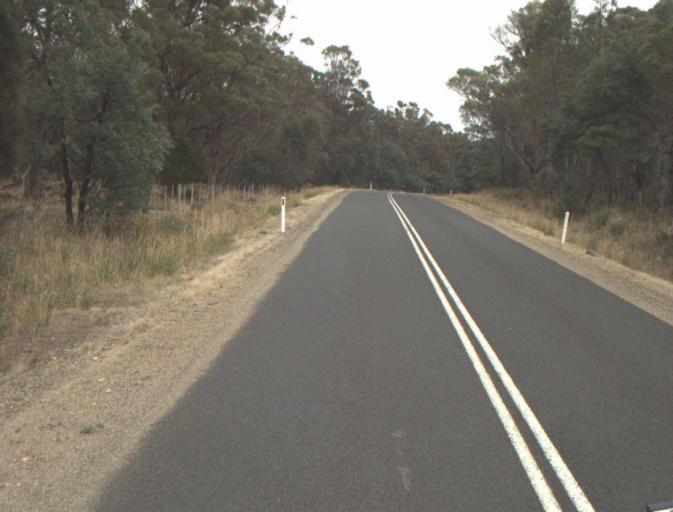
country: AU
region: Tasmania
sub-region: Northern Midlands
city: Evandale
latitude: -41.5130
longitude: 147.3392
